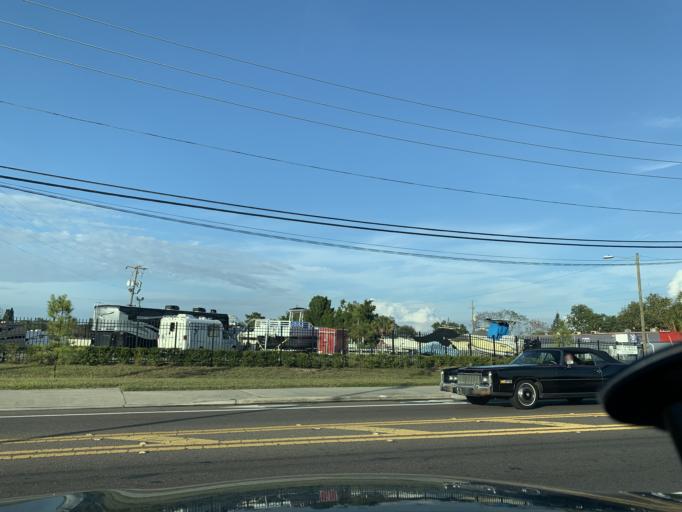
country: US
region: Florida
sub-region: Pinellas County
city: Ridgecrest
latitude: 27.8801
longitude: -82.7999
